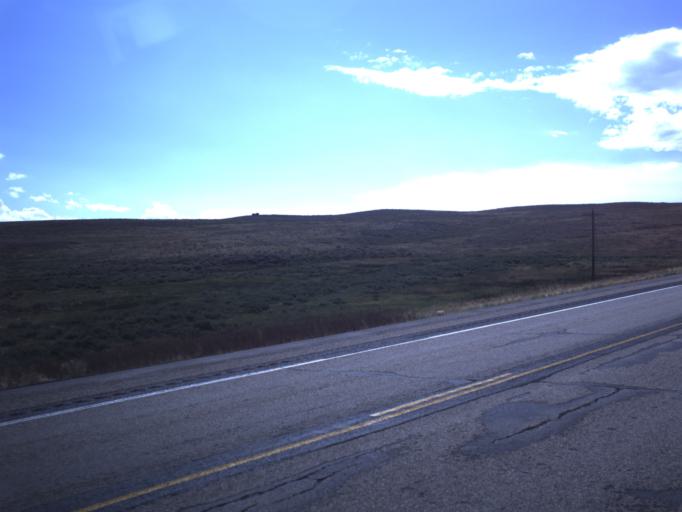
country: US
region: Utah
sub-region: Wasatch County
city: Heber
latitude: 40.1881
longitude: -111.0693
